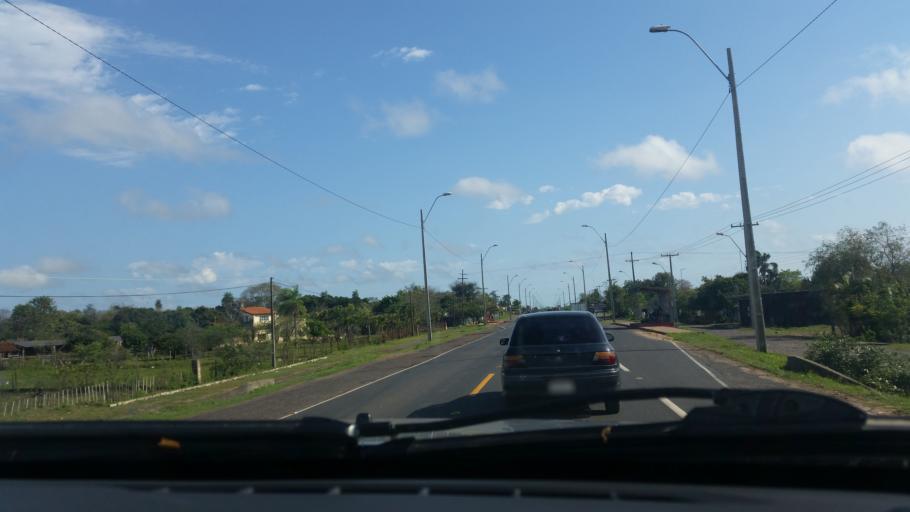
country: PY
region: Presidente Hayes
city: Benjamin Aceval
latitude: -24.9560
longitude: -57.5493
